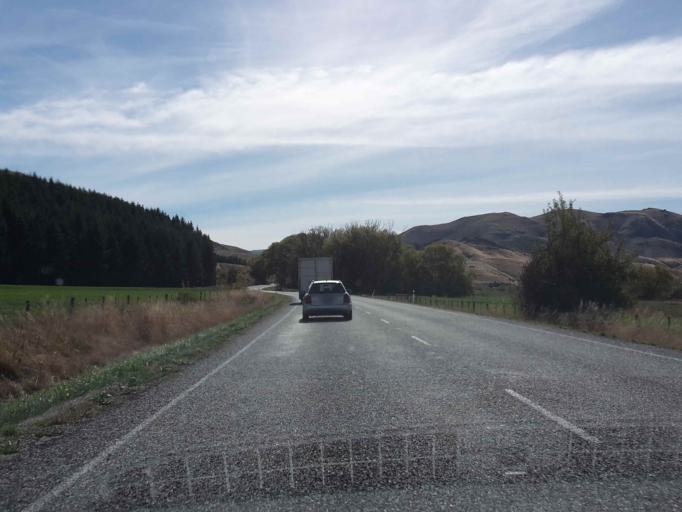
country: NZ
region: Otago
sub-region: Queenstown-Lakes District
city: Wanaka
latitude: -44.7668
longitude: 169.5086
